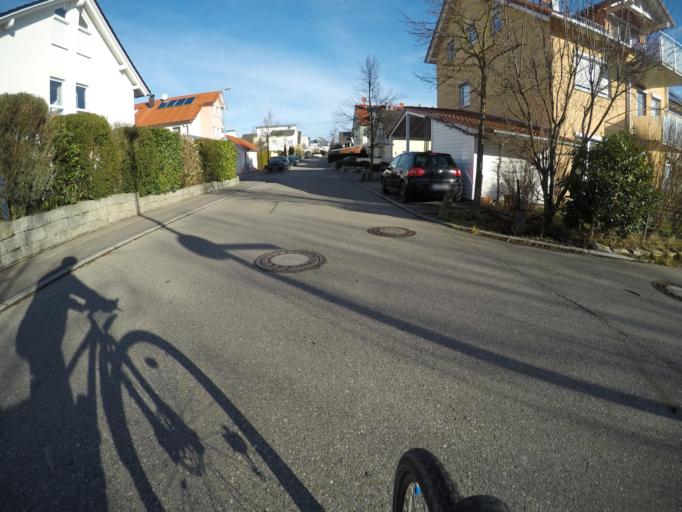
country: DE
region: Baden-Wuerttemberg
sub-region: Regierungsbezirk Stuttgart
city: Gartringen
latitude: 48.6459
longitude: 8.9075
